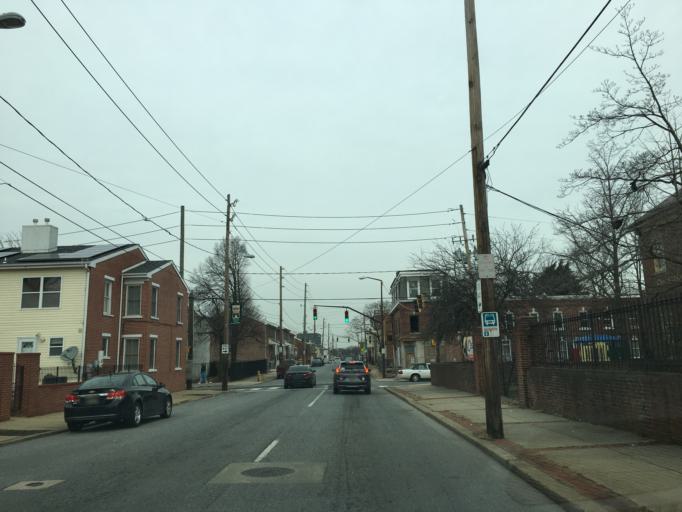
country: US
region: Delaware
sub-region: New Castle County
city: Wilmington
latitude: 39.7388
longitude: -75.5414
